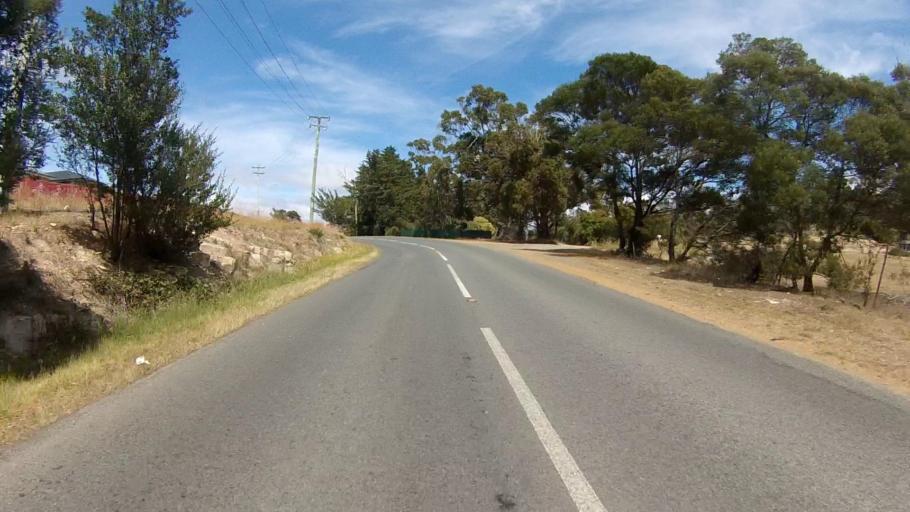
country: AU
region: Tasmania
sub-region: Clarence
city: Lindisfarne
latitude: -42.8211
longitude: 147.3505
